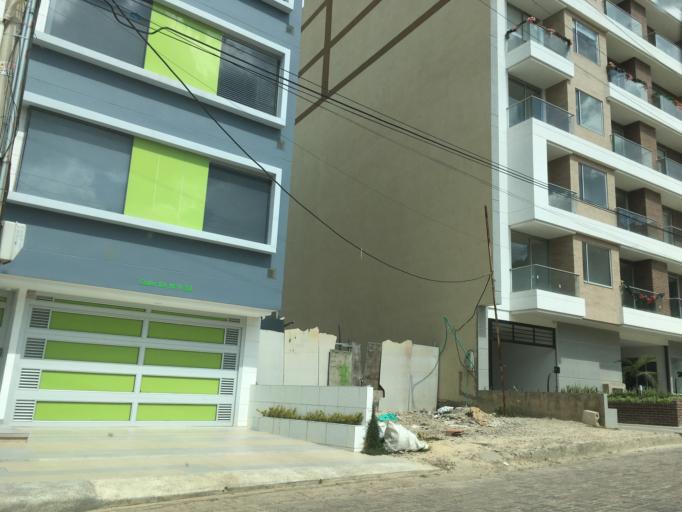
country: CO
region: Boyaca
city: Sogamoso
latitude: 5.7247
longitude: -72.9203
